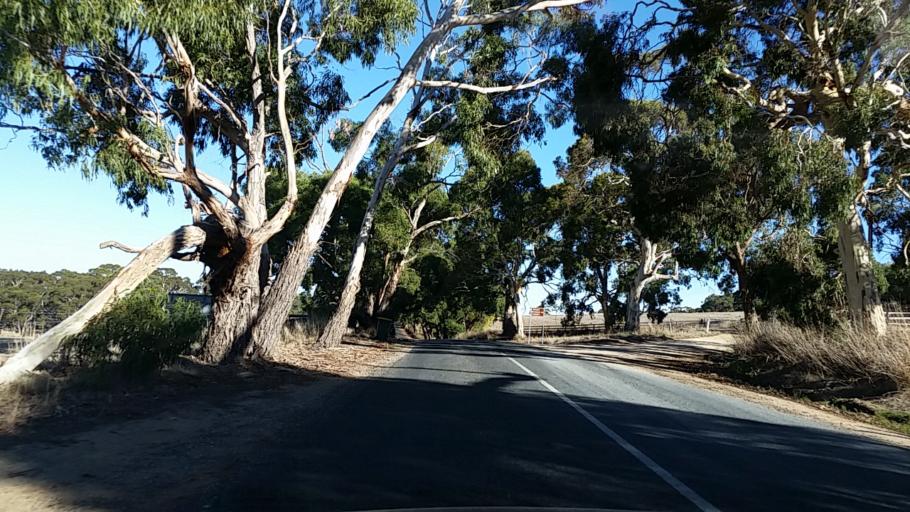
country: AU
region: South Australia
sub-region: Mount Barker
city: Nairne
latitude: -35.0597
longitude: 138.9251
